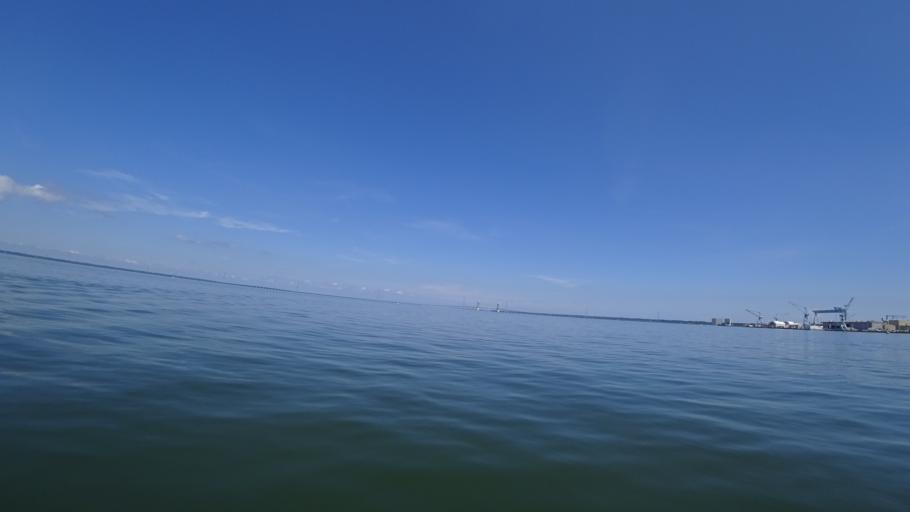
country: US
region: Virginia
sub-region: City of Newport News
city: Newport News
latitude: 36.9849
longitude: -76.4514
